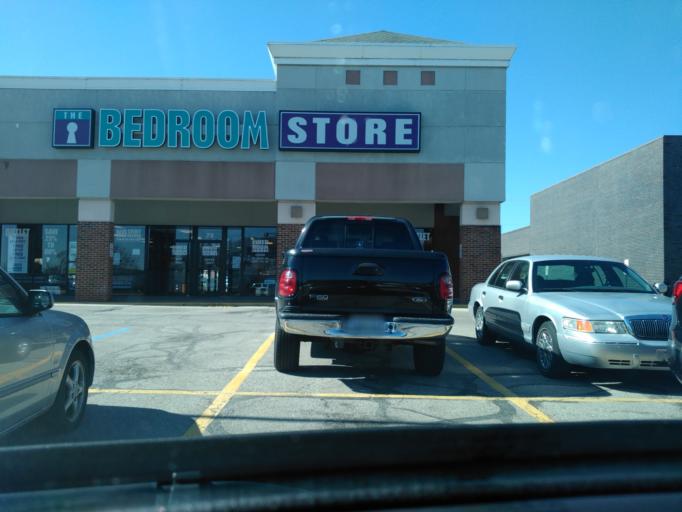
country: US
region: Missouri
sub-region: Saint Louis County
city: Fenton
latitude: 38.5118
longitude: -90.4437
